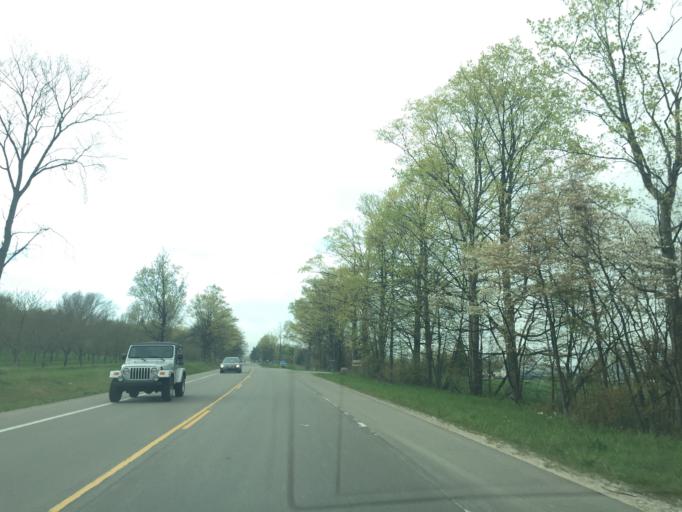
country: US
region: Michigan
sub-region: Leelanau County
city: Leland
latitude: 45.0733
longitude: -85.5888
